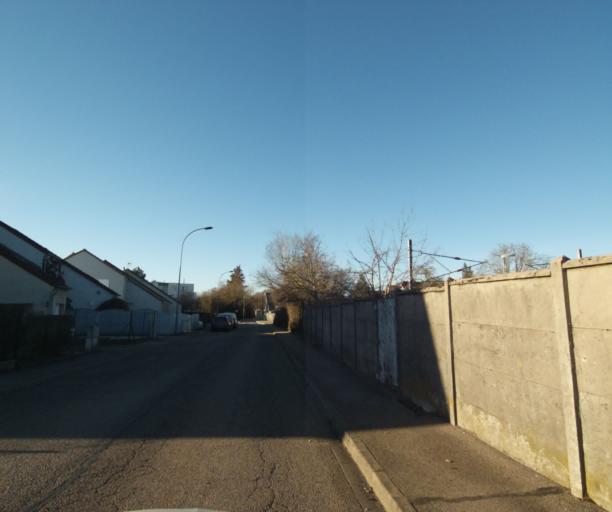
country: FR
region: Lorraine
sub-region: Departement de Meurthe-et-Moselle
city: Laneuveville-devant-Nancy
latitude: 48.6548
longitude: 6.2286
